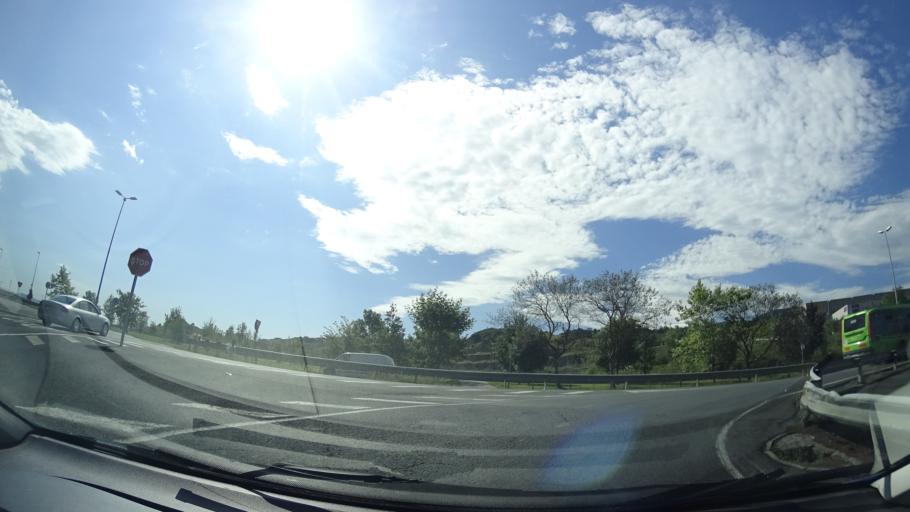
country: ES
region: Basque Country
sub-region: Bizkaia
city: Urtuella
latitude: 43.3111
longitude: -3.0767
